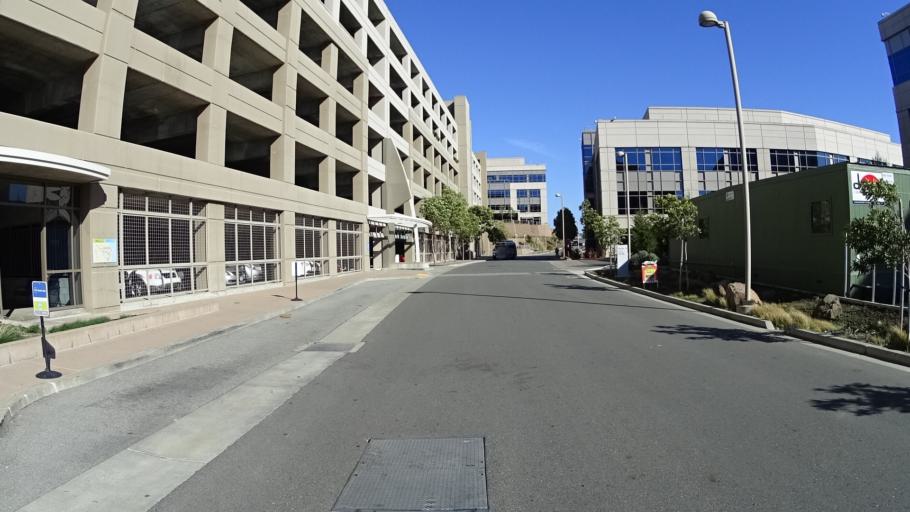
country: US
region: California
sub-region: San Mateo County
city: South San Francisco
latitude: 37.6519
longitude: -122.3830
